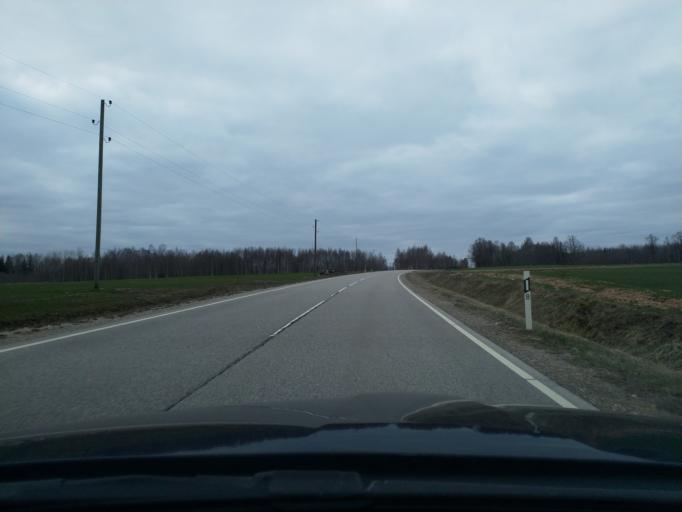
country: LV
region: Talsu Rajons
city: Sabile
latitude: 56.9445
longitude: 22.4828
